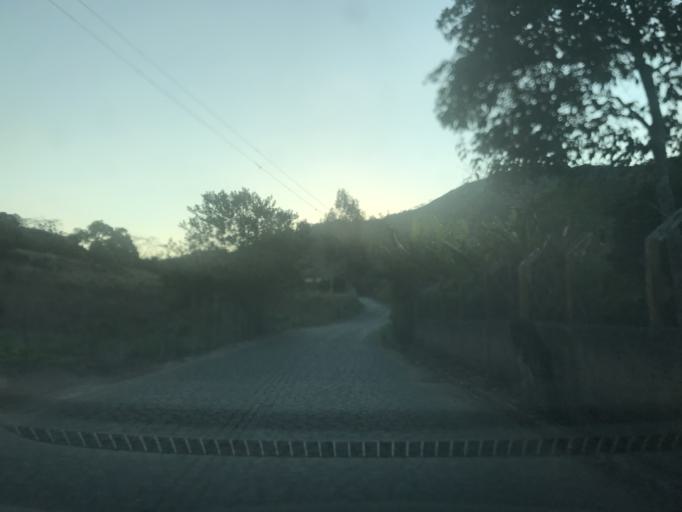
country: BR
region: Pernambuco
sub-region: Bezerros
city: Bezerros
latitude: -8.1834
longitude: -35.7655
